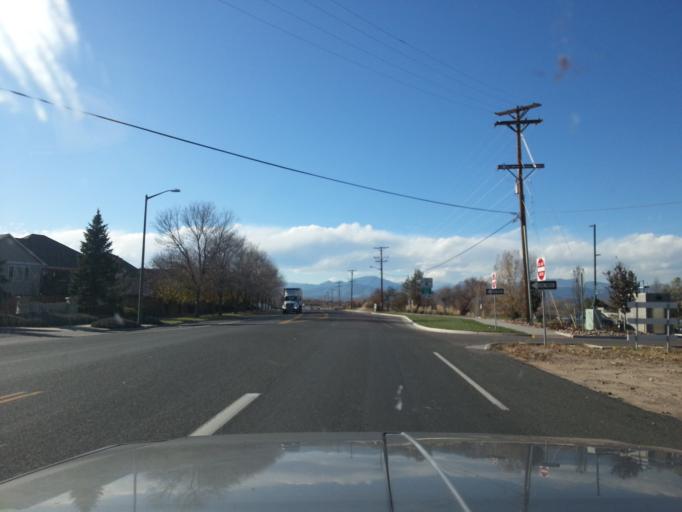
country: US
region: Colorado
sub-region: Larimer County
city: Loveland
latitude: 40.3926
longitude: -105.1111
